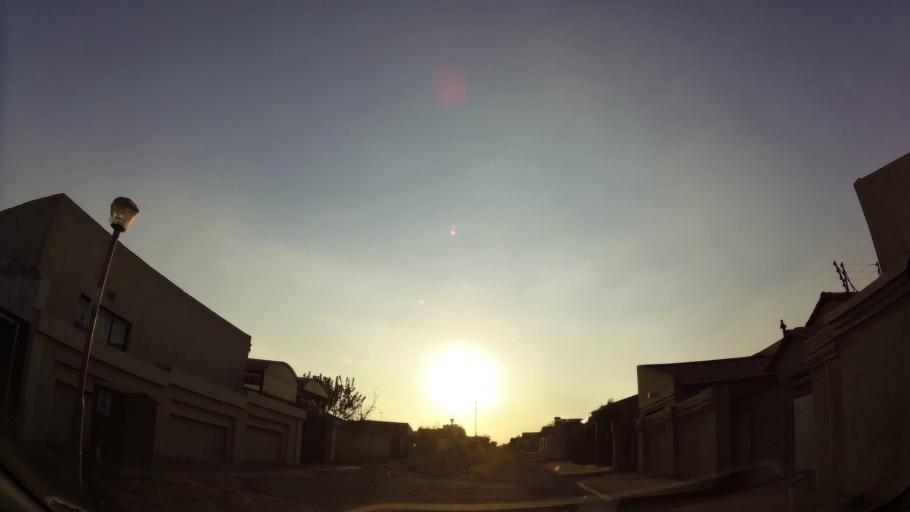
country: ZA
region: Gauteng
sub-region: Ekurhuleni Metropolitan Municipality
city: Benoni
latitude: -26.1638
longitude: 28.3816
